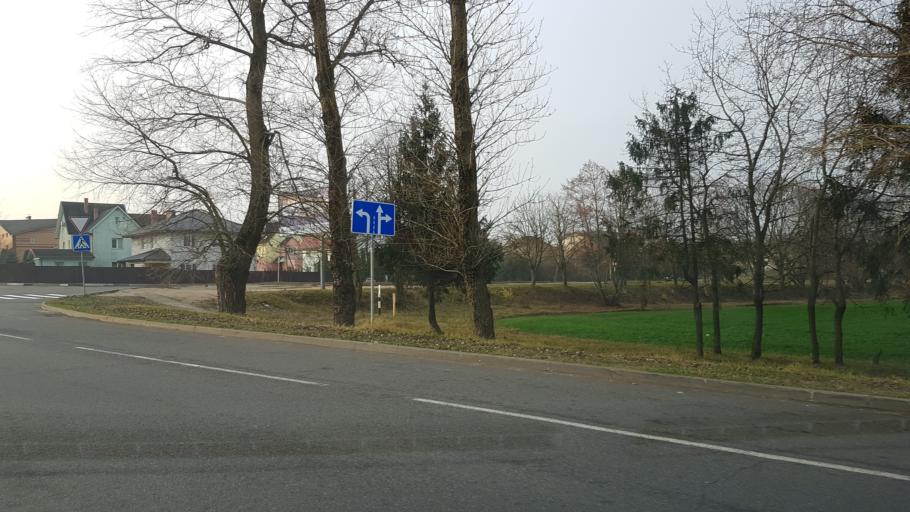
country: BY
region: Minsk
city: Bal'shavik
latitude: 53.9635
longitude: 27.5350
